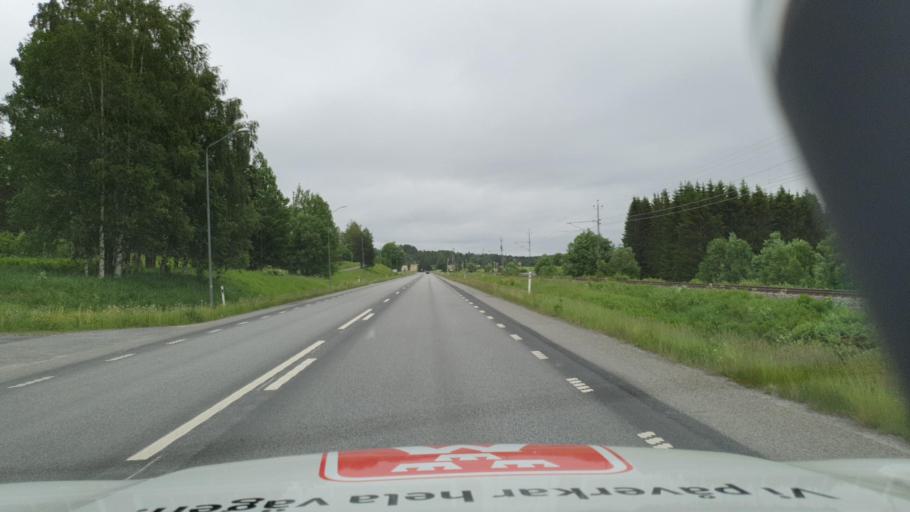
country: SE
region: Jaemtland
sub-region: Are Kommun
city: Jarpen
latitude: 63.3092
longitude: 13.6280
